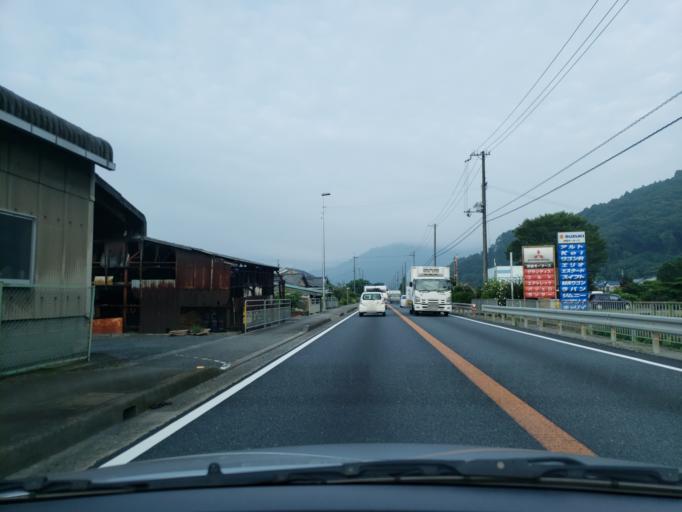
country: JP
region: Hyogo
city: Kariya
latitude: 34.8270
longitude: 134.3784
